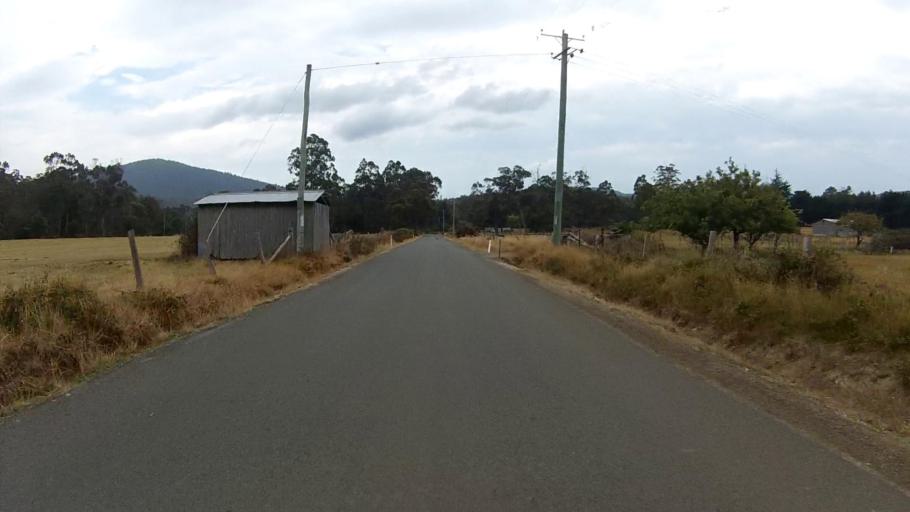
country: AU
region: Tasmania
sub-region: Huon Valley
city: Cygnet
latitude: -43.2398
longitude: 147.1529
